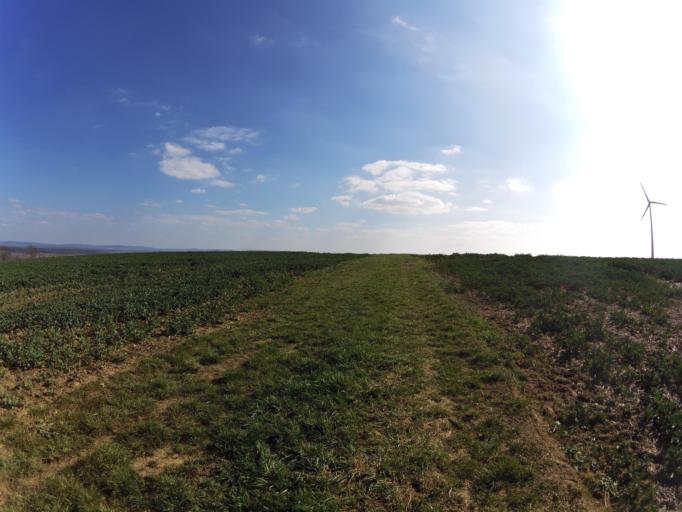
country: DE
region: Bavaria
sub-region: Regierungsbezirk Unterfranken
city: Nordheim
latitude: 49.8374
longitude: 10.1681
